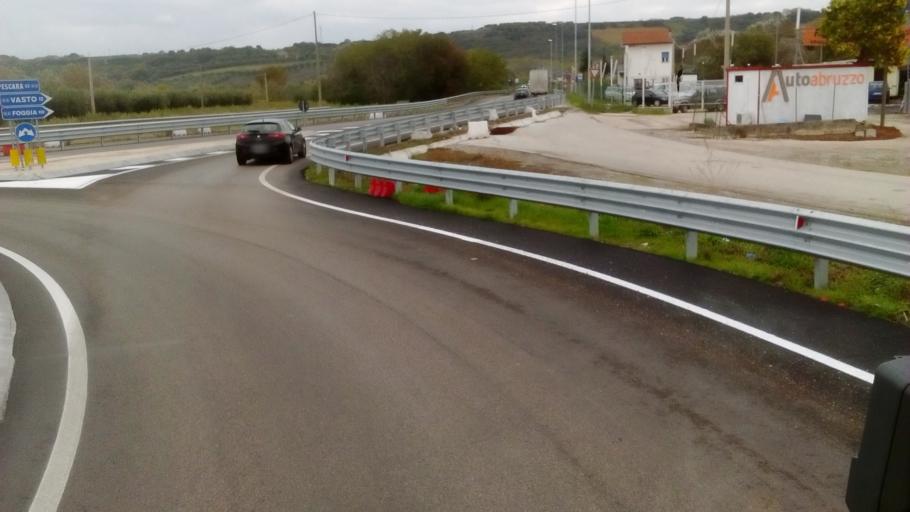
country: IT
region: Abruzzo
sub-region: Provincia di Chieti
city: Casalbordino-Miracoli
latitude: 42.1639
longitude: 14.6409
